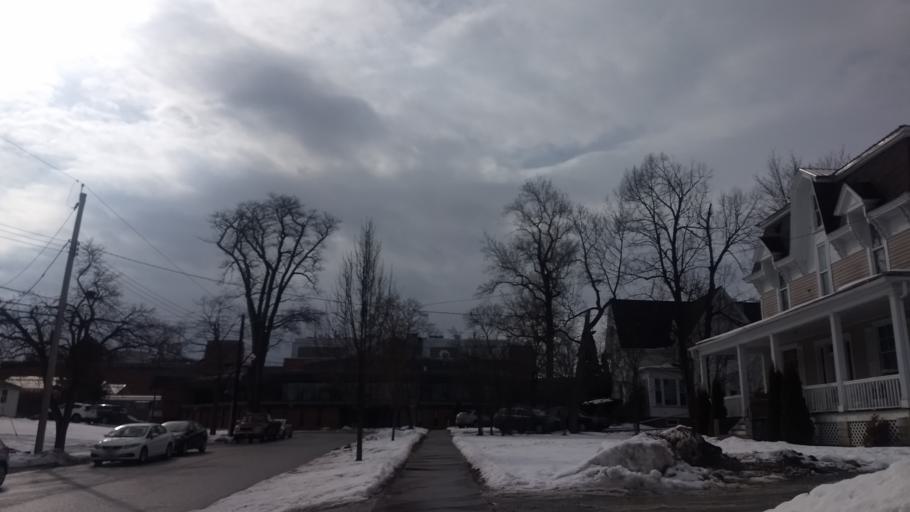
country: US
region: New York
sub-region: Livingston County
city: Geneseo
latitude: 42.7986
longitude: -77.8187
